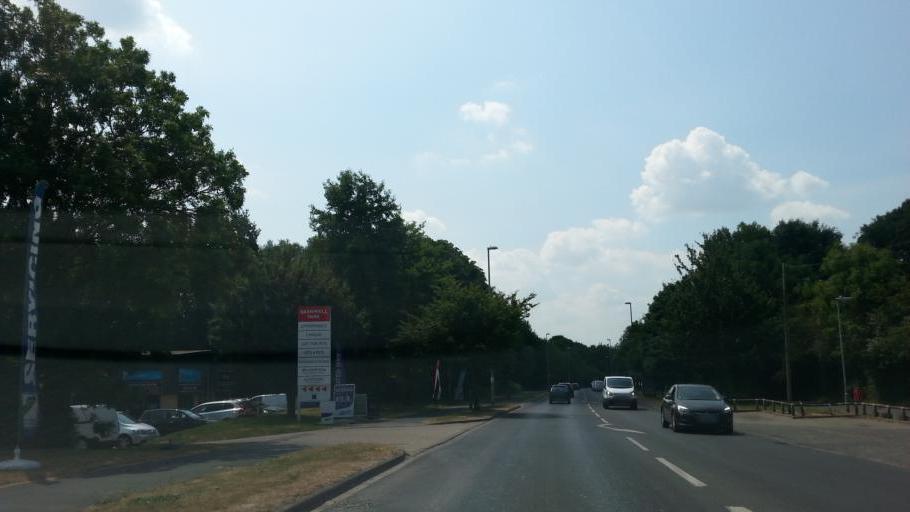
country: GB
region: England
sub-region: Cambridgeshire
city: Cambridge
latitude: 52.2046
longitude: 0.1634
